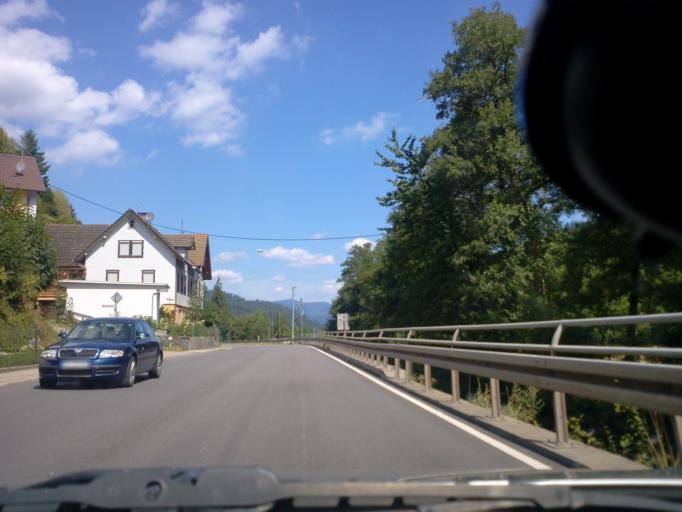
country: DE
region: Baden-Wuerttemberg
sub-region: Freiburg Region
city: Hornberg
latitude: 48.2260
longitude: 8.2219
